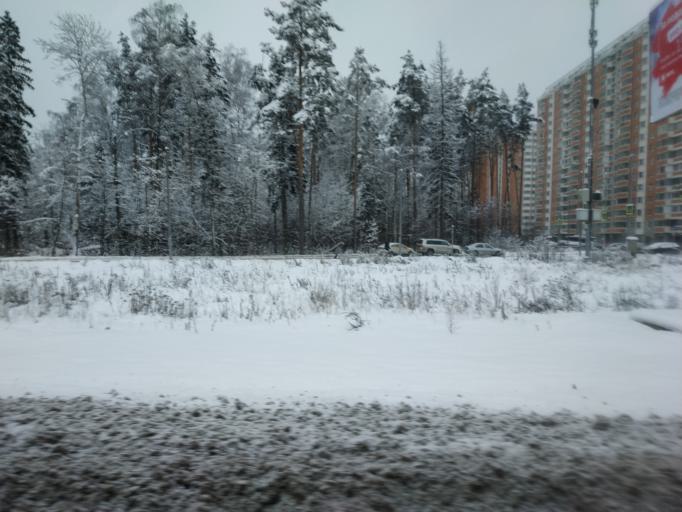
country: RU
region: Moscow
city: Vostochnyy
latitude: 55.8242
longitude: 37.8824
